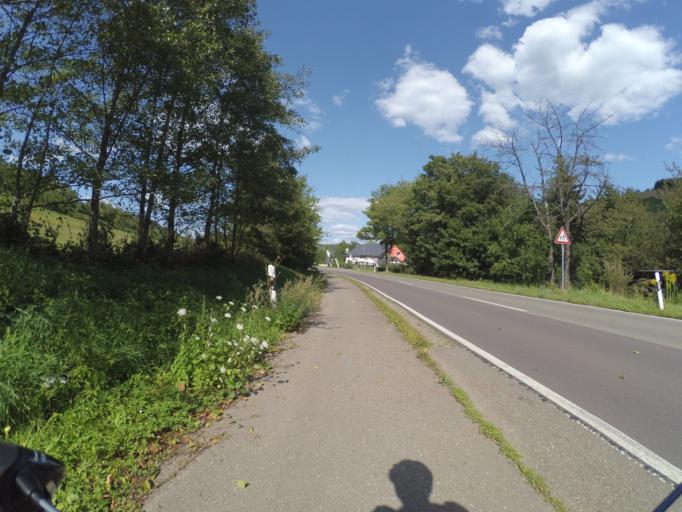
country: DE
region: Rheinland-Pfalz
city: Longuich
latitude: 49.7844
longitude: 6.7739
